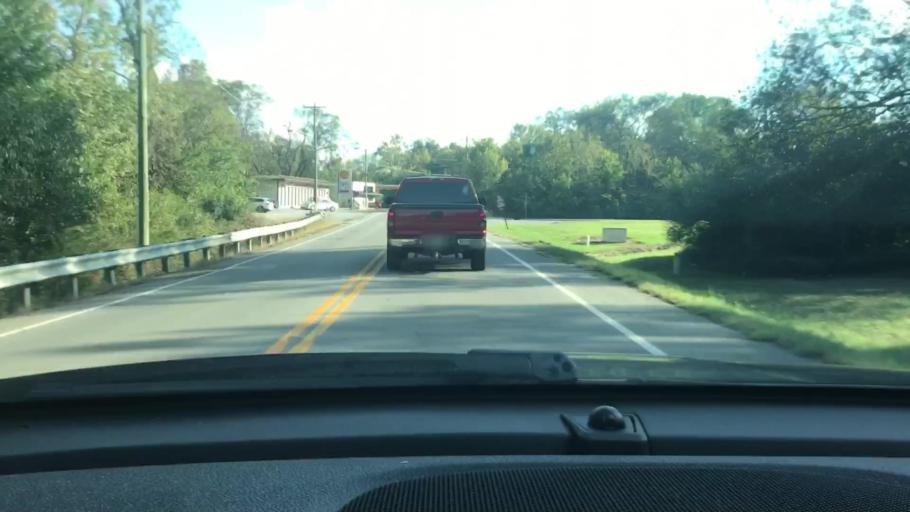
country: US
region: Tennessee
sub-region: Sumner County
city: Shackle Island
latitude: 36.3748
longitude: -86.6176
